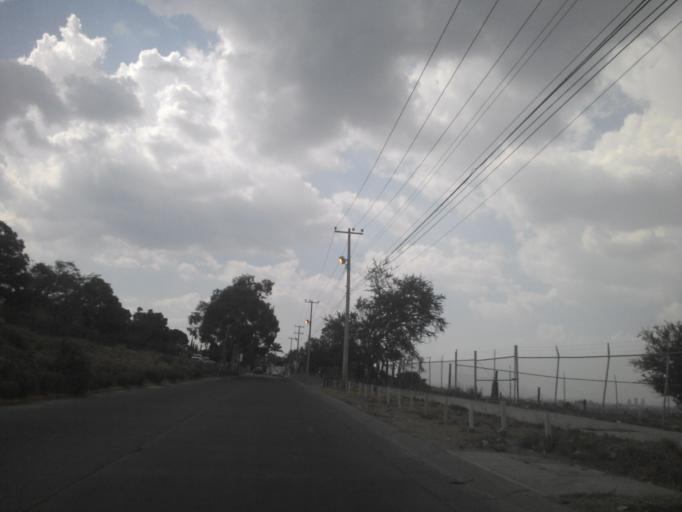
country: MX
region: Jalisco
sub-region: Tlajomulco de Zuniga
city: La Tijera
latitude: 20.6157
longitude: -103.4015
